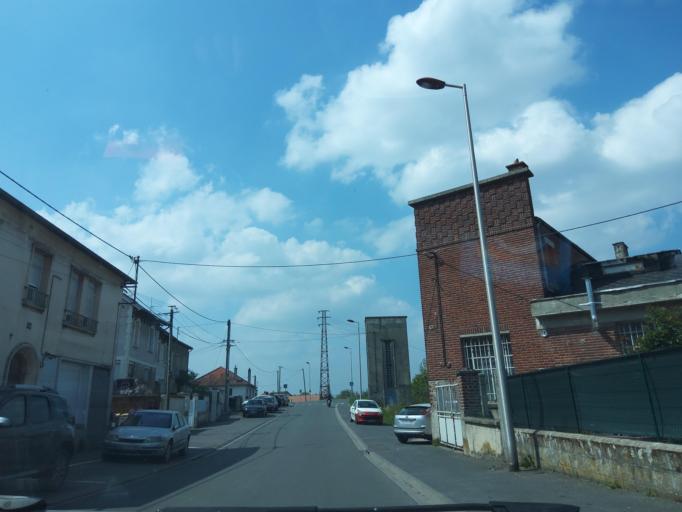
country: FR
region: Picardie
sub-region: Departement de l'Aisne
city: Laon
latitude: 49.5703
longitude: 3.6145
